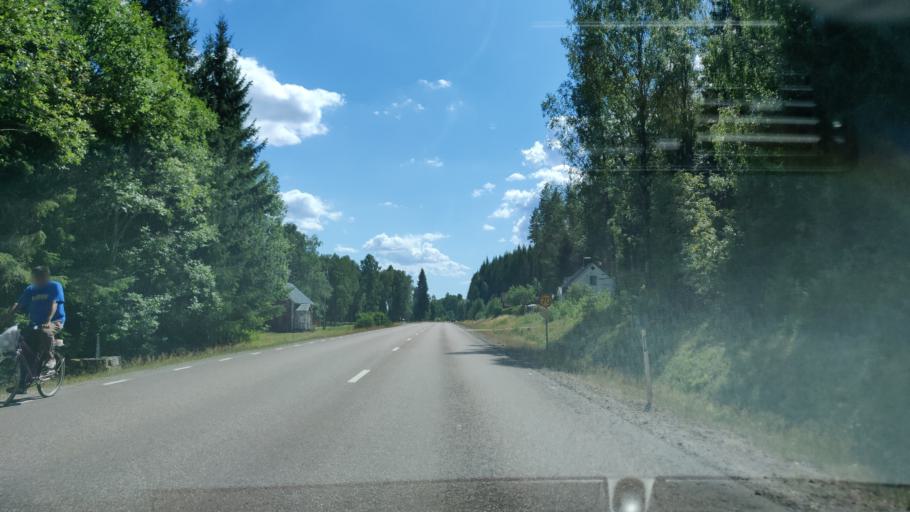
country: SE
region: Vaermland
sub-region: Hagfors Kommun
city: Ekshaerad
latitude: 60.1914
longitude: 13.4976
